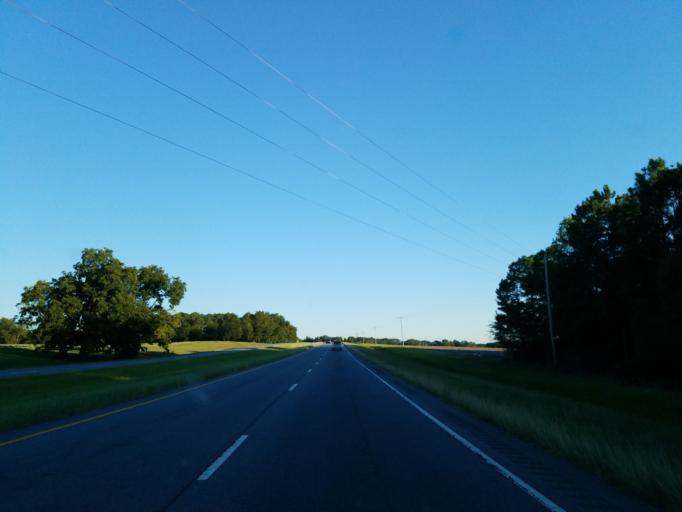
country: US
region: Georgia
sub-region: Worth County
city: Sylvester
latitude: 31.4936
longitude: -83.7073
